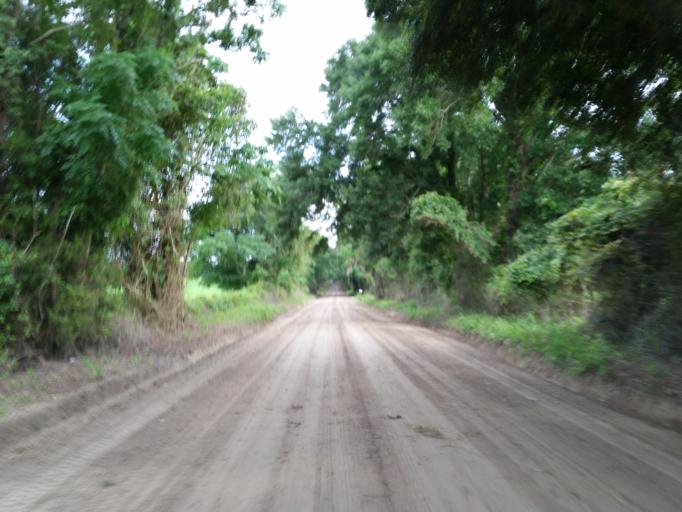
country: US
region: Florida
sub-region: Alachua County
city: High Springs
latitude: 29.9615
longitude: -82.5595
